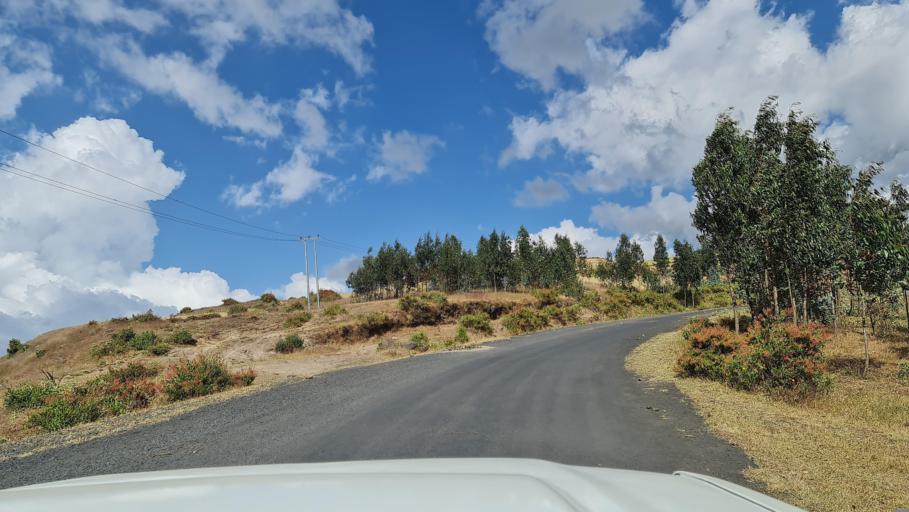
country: ET
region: Amhara
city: Debark'
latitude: 13.1355
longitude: 37.9327
